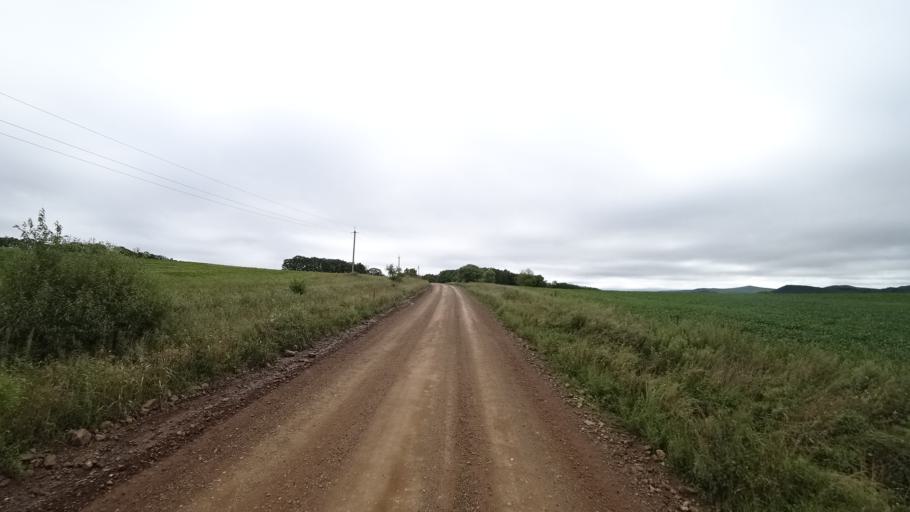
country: RU
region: Primorskiy
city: Lyalichi
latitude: 44.0622
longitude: 132.4775
